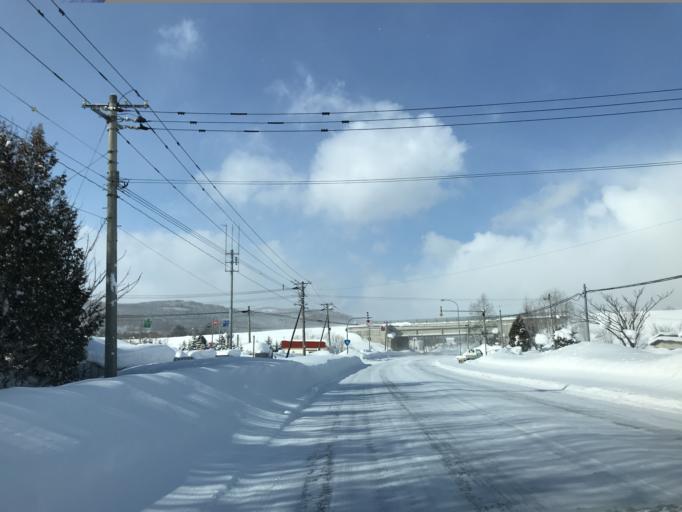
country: JP
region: Hokkaido
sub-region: Asahikawa-shi
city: Asahikawa
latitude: 43.9214
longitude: 142.4789
